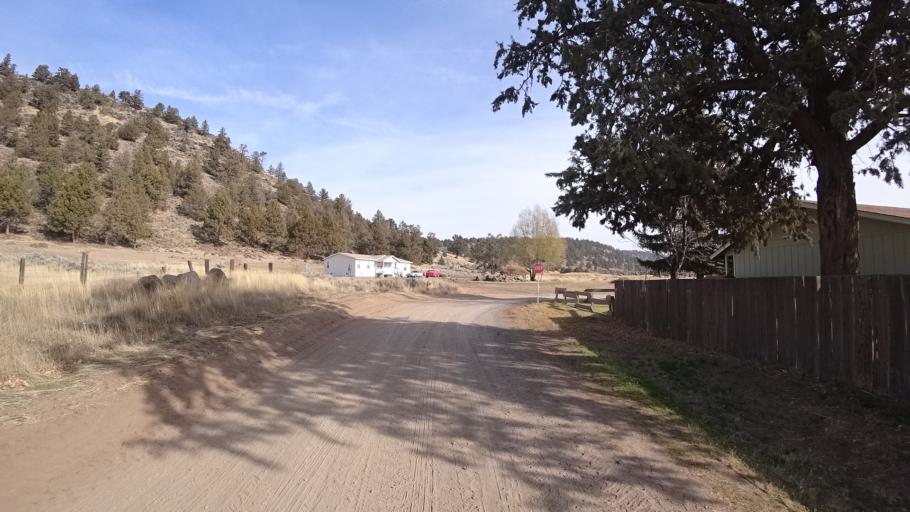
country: US
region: Oregon
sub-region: Klamath County
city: Klamath Falls
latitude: 41.9717
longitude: -121.9138
